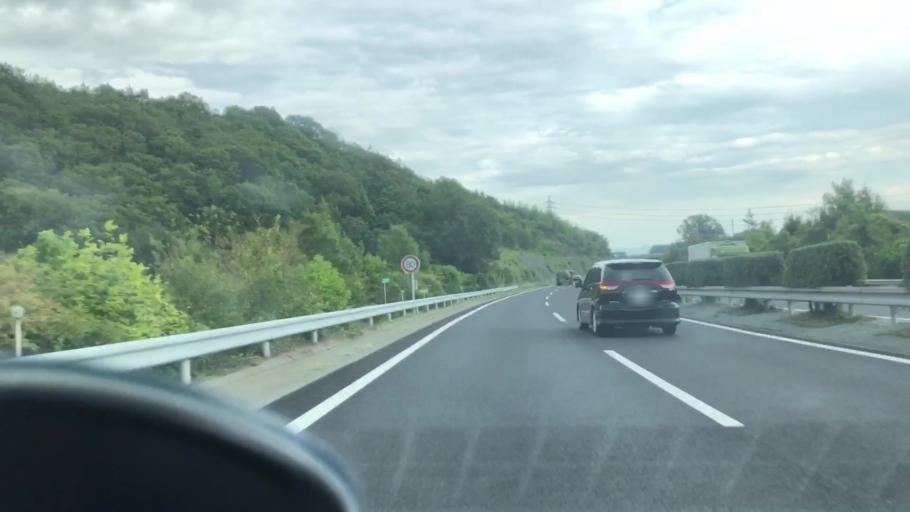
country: JP
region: Hyogo
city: Yashiro
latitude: 34.9391
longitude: 134.8792
